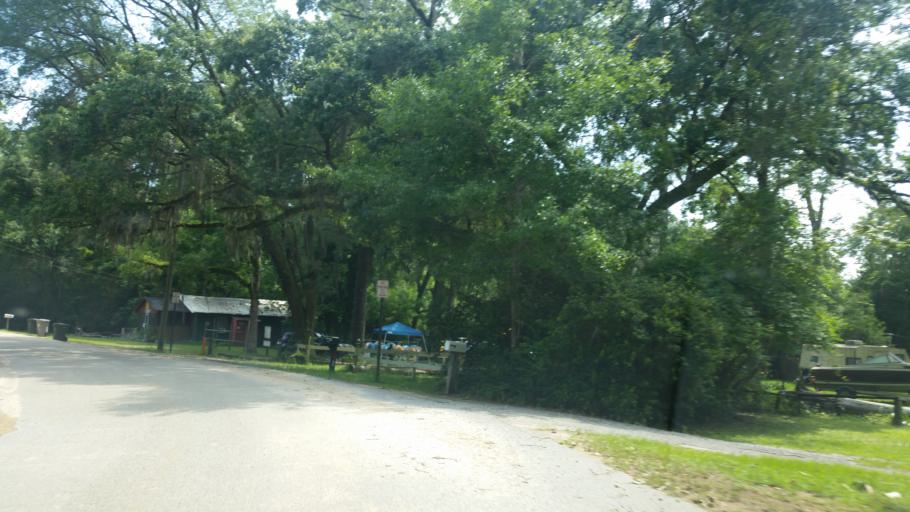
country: US
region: Florida
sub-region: Escambia County
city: Cantonment
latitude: 30.6059
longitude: -87.3974
